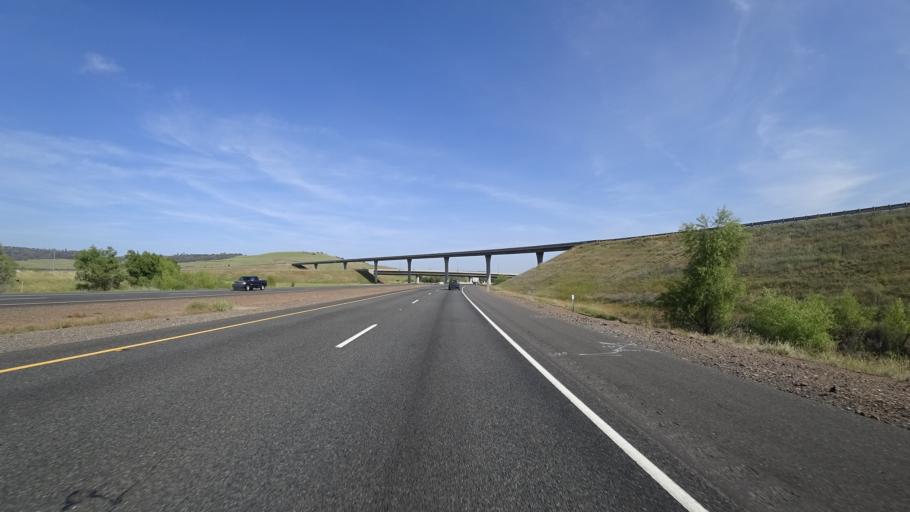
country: US
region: California
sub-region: Butte County
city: Thermalito
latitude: 39.5839
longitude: -121.6254
